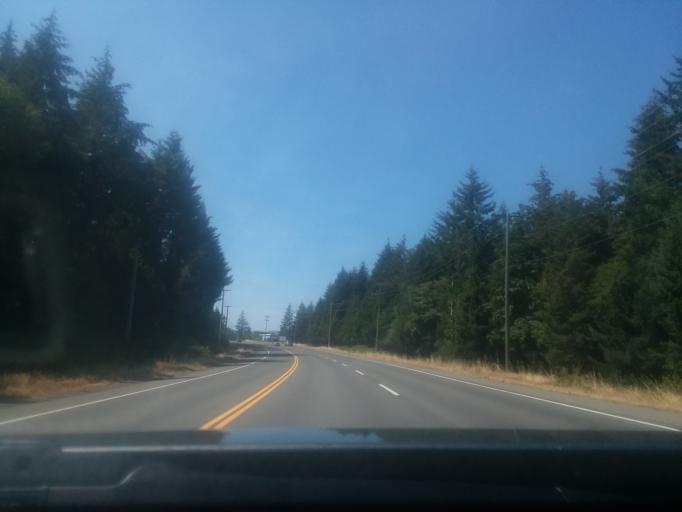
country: CA
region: British Columbia
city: Courtenay
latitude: 49.7152
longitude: -124.9537
